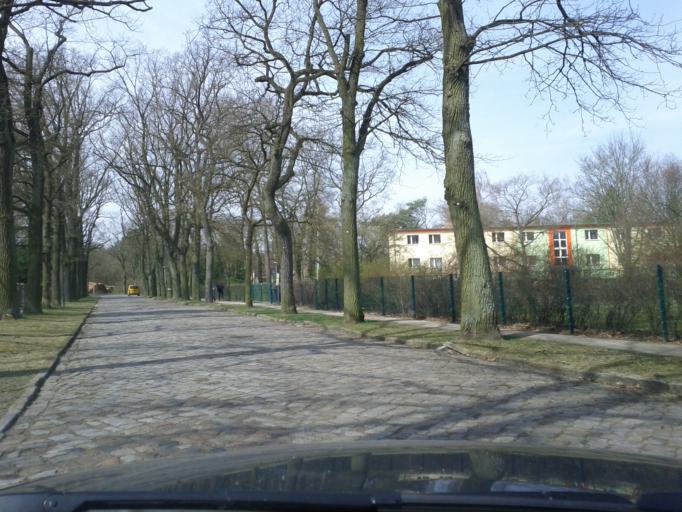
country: DE
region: Brandenburg
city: Schoneiche
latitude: 52.4686
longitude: 13.6811
